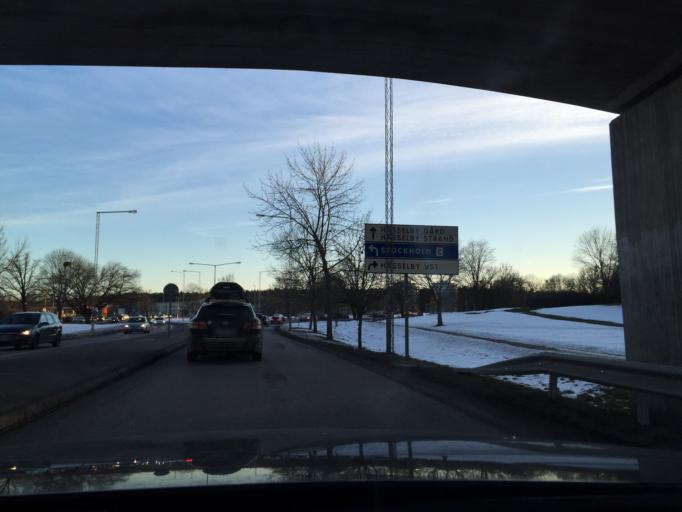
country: SE
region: Stockholm
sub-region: Jarfalla Kommun
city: Jakobsberg
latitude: 59.3680
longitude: 17.8603
